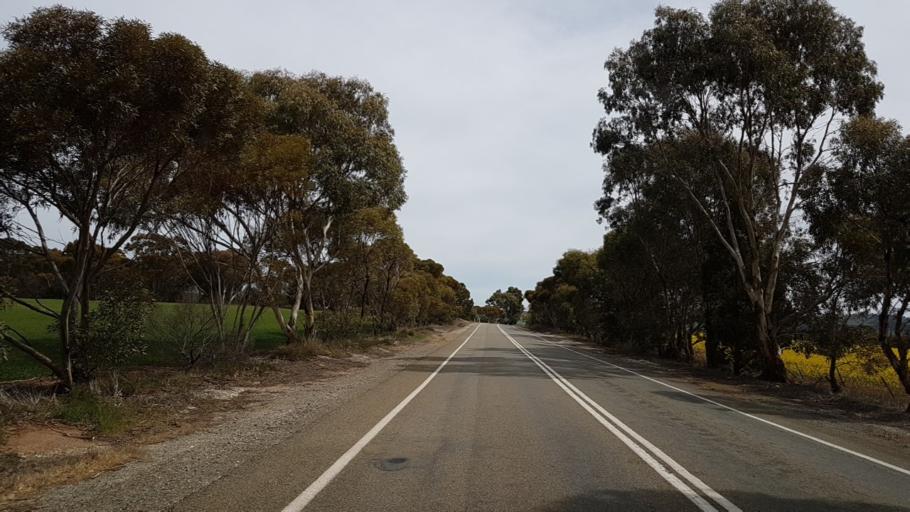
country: AU
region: South Australia
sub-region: Northern Areas
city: Jamestown
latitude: -33.0401
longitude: 138.6347
